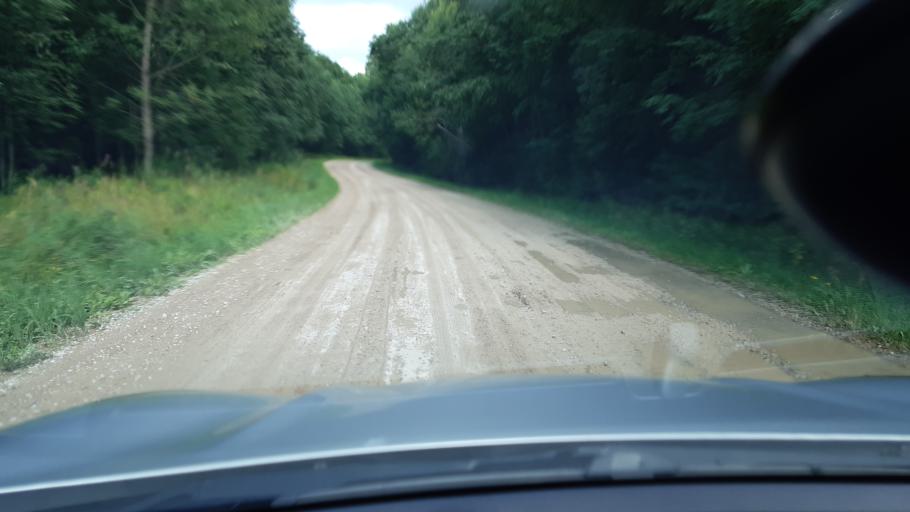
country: EE
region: Jaervamaa
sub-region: Tueri vald
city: Tueri
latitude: 58.9262
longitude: 25.2152
